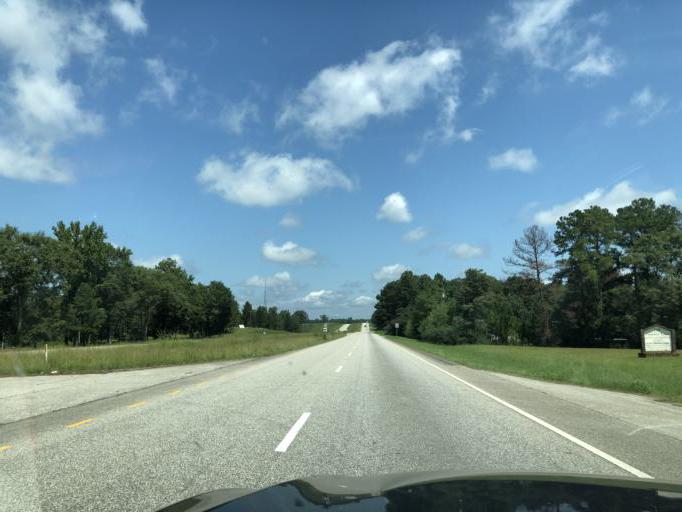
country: US
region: Alabama
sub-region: Henry County
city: Abbeville
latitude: 31.7036
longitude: -85.2763
